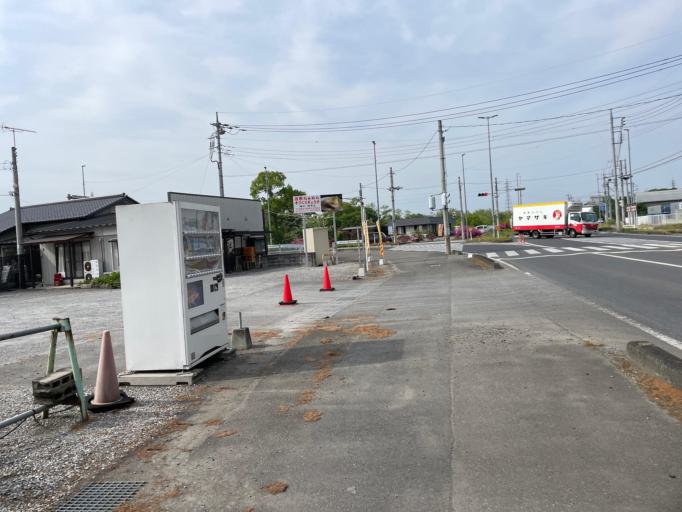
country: JP
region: Tochigi
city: Mibu
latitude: 36.4056
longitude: 139.8040
